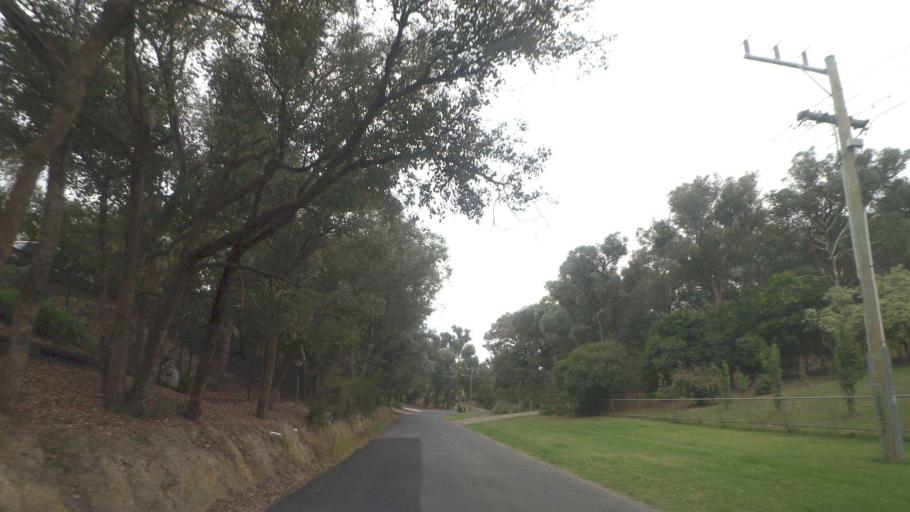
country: AU
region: Victoria
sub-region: Nillumbik
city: North Warrandyte
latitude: -37.7446
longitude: 145.1839
